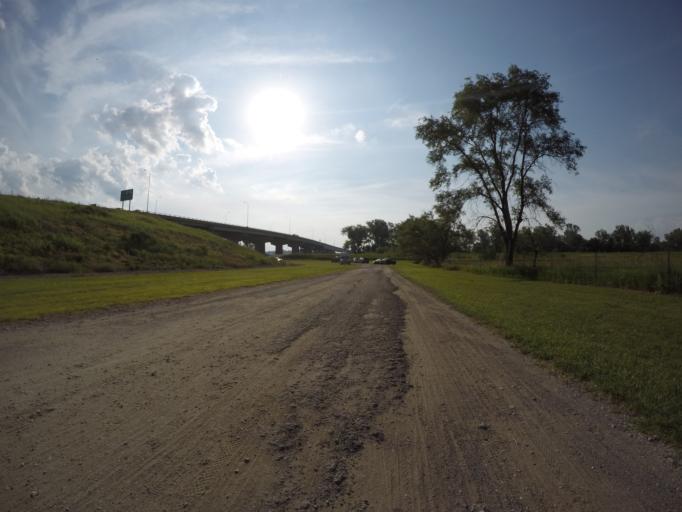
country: US
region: Kansas
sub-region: Doniphan County
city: Elwood
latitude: 39.7489
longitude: -94.8650
